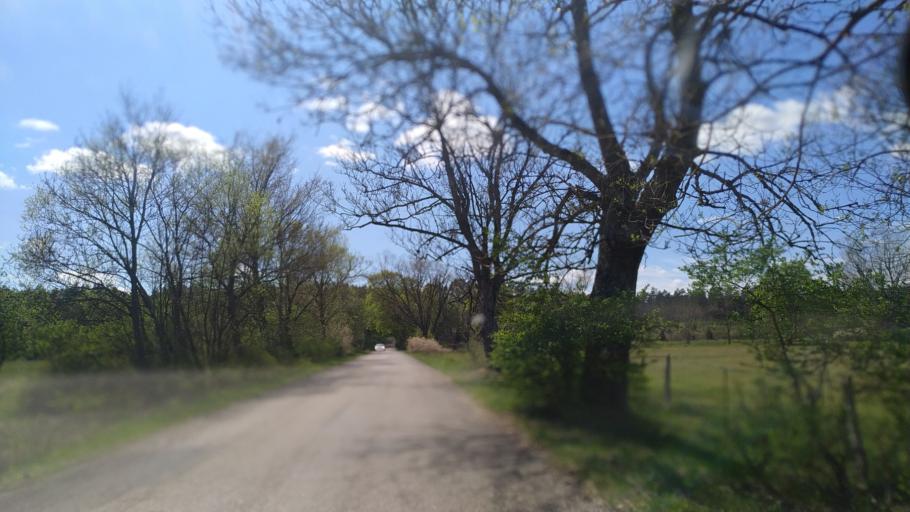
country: PL
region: Greater Poland Voivodeship
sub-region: Powiat pilski
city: Pila
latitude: 53.2560
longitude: 16.7454
